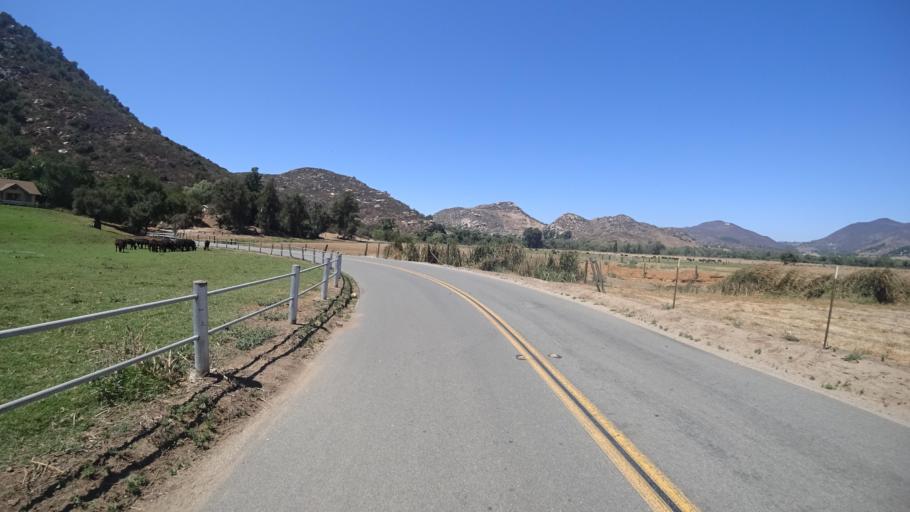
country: US
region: California
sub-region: San Diego County
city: Rainbow
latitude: 33.3340
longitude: -117.1285
